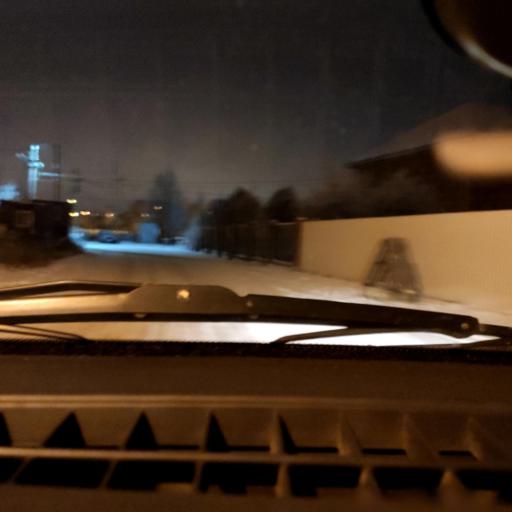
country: RU
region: Bashkortostan
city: Ufa
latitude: 54.7682
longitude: 55.9490
